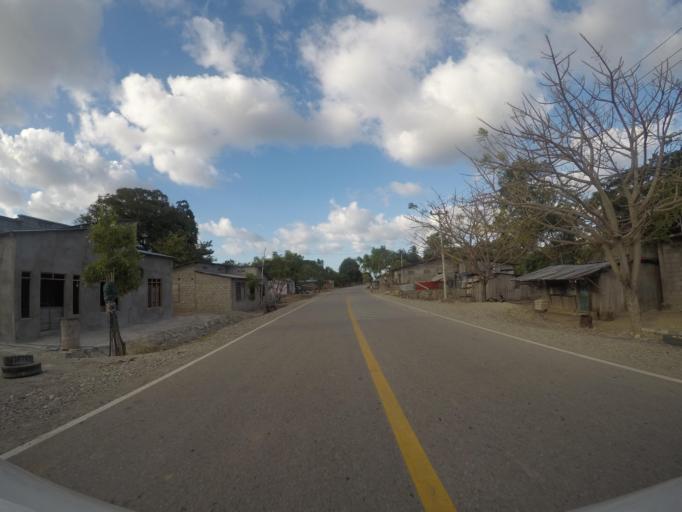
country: TL
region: Lautem
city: Lospalos
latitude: -8.4010
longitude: 126.8314
